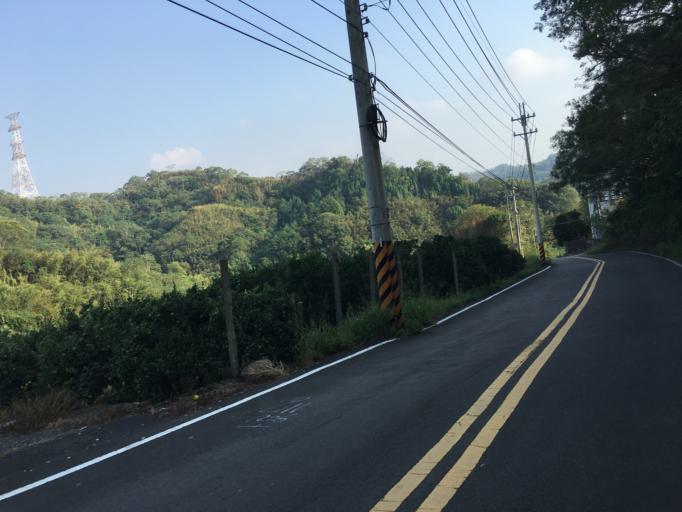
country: TW
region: Taiwan
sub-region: Hsinchu
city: Hsinchu
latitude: 24.7354
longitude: 121.0266
